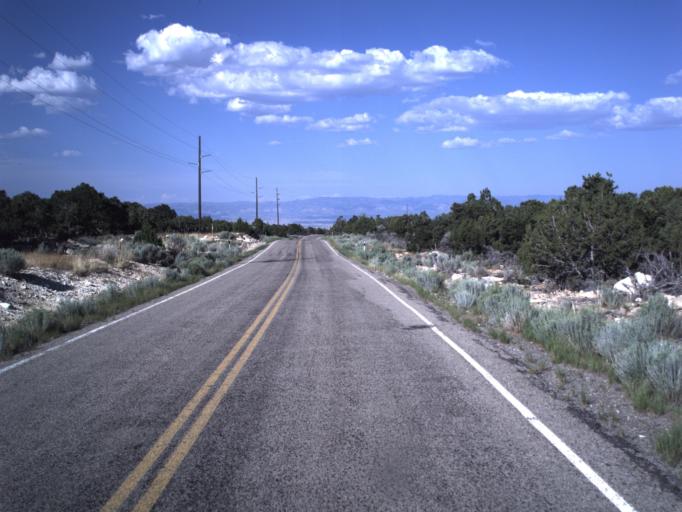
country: US
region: Utah
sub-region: Emery County
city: Huntington
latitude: 39.4845
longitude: -110.9642
